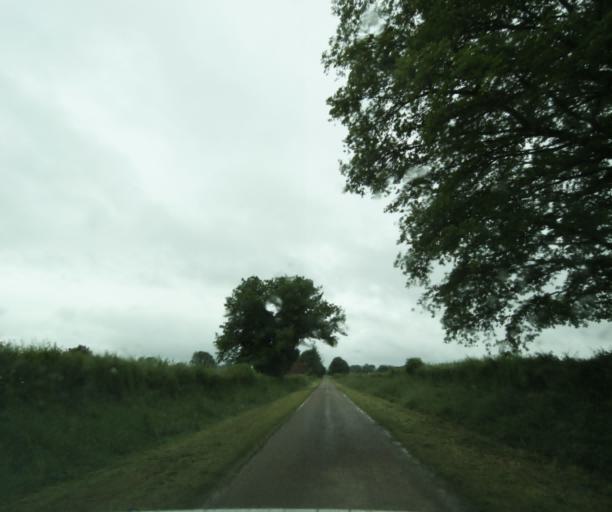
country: FR
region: Bourgogne
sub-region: Departement de Saone-et-Loire
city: Charolles
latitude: 46.4731
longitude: 4.2954
